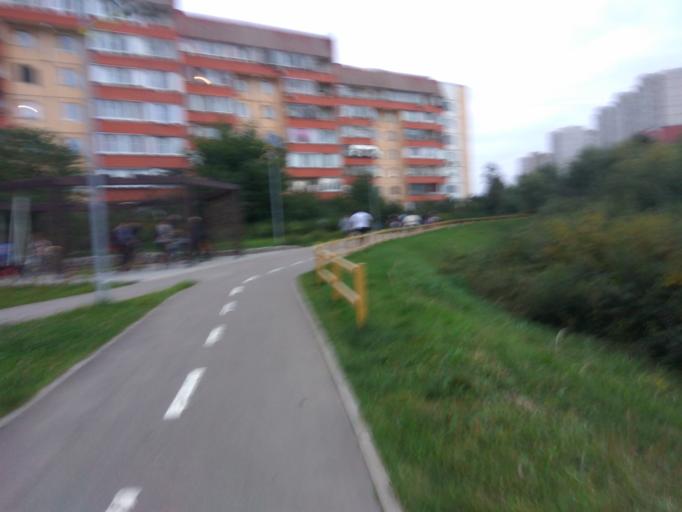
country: RU
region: Moskovskaya
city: Kuskovo
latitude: 55.7344
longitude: 37.8493
